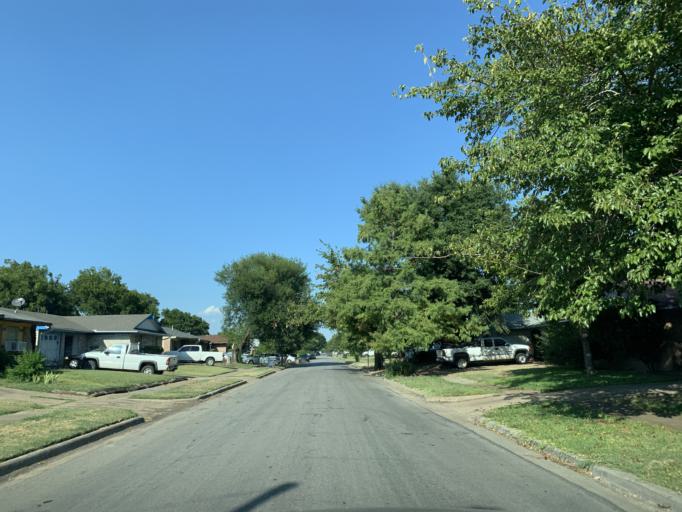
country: US
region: Texas
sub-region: Dallas County
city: Hutchins
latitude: 32.6639
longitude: -96.7698
